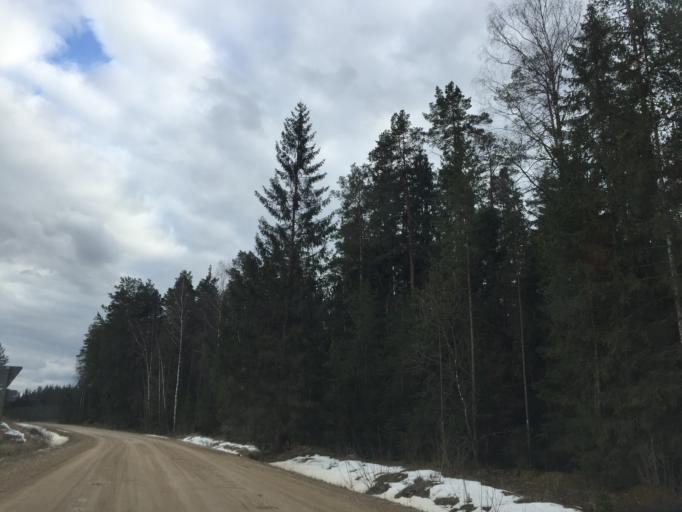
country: LV
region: Ogre
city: Jumprava
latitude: 56.5924
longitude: 24.9875
